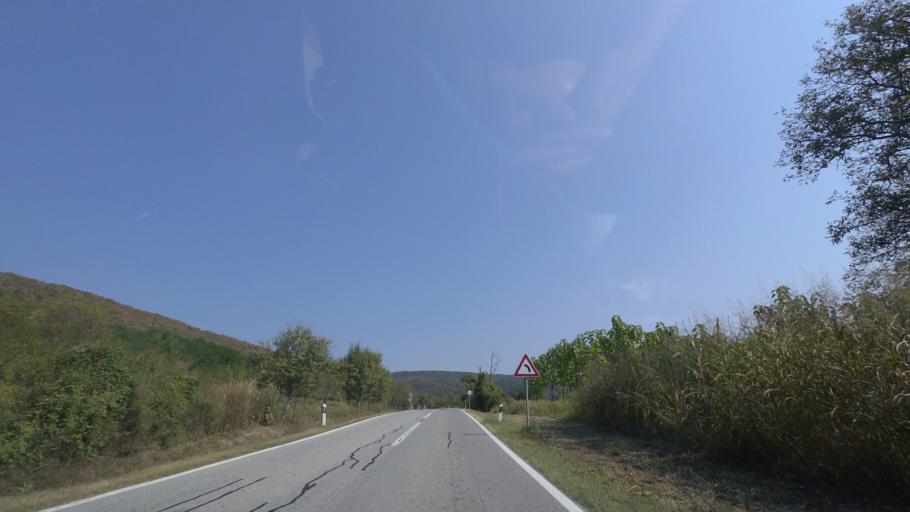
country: HR
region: Pozesko-Slavonska
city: Velika
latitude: 45.4188
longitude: 17.5027
